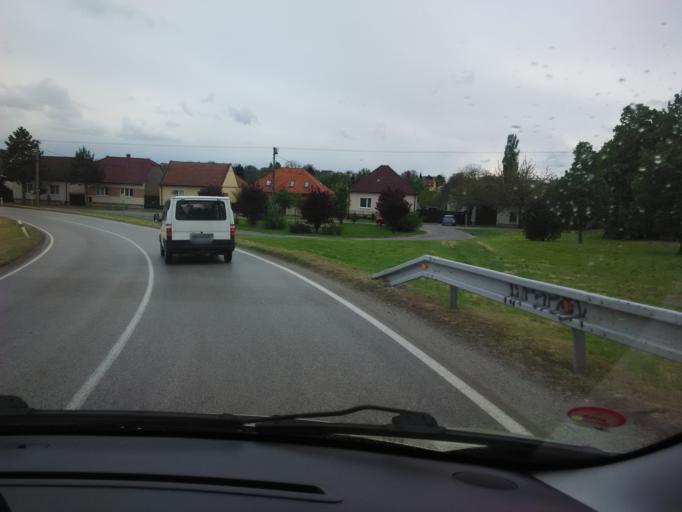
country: SK
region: Trnavsky
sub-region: Okres Trnava
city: Trnava
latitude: 48.4449
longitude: 17.6063
